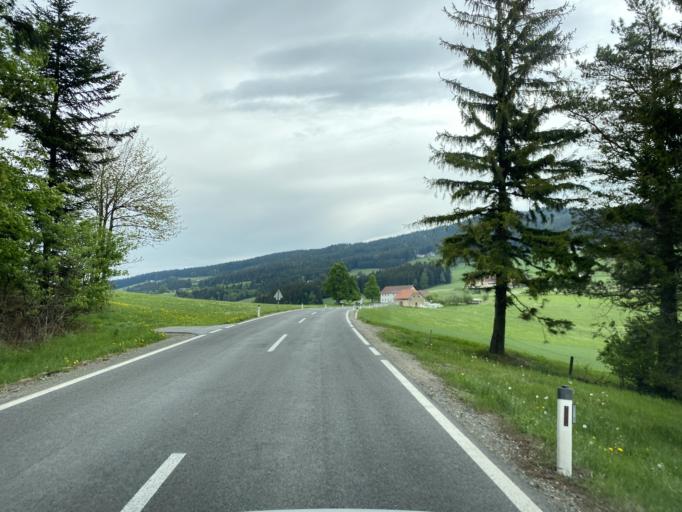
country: AT
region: Styria
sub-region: Politischer Bezirk Weiz
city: Gschaid bei Birkfeld
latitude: 47.3370
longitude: 15.7465
